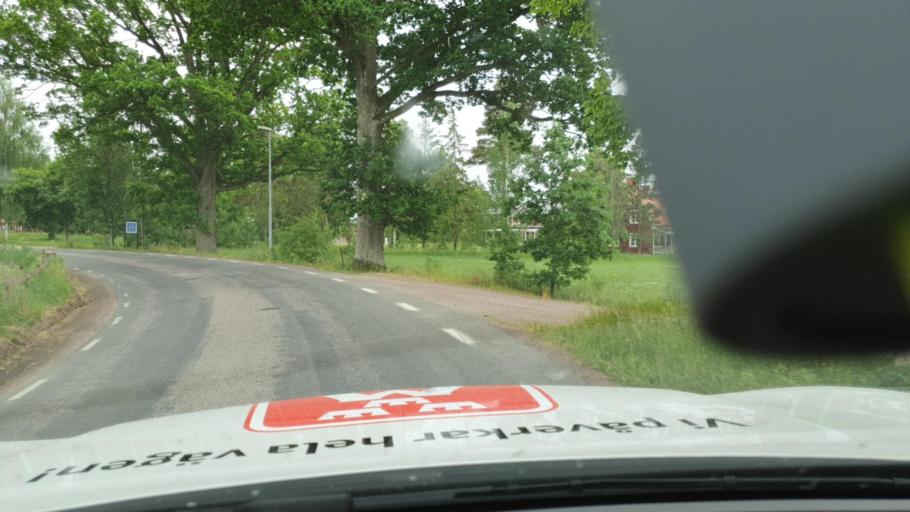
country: SE
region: Vaestra Goetaland
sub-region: Tidaholms Kommun
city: Olofstorp
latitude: 58.3381
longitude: 14.0465
